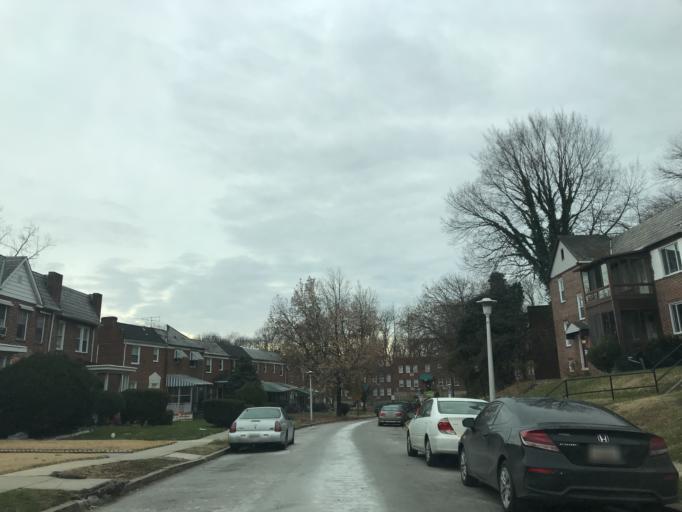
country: US
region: Maryland
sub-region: City of Baltimore
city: Baltimore
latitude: 39.3190
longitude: -76.6601
